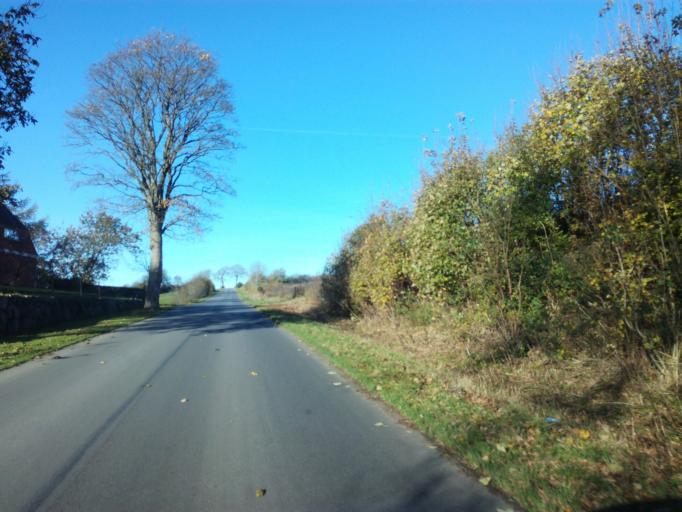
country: DK
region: South Denmark
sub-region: Vejle Kommune
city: Vejle
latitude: 55.6644
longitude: 9.5829
